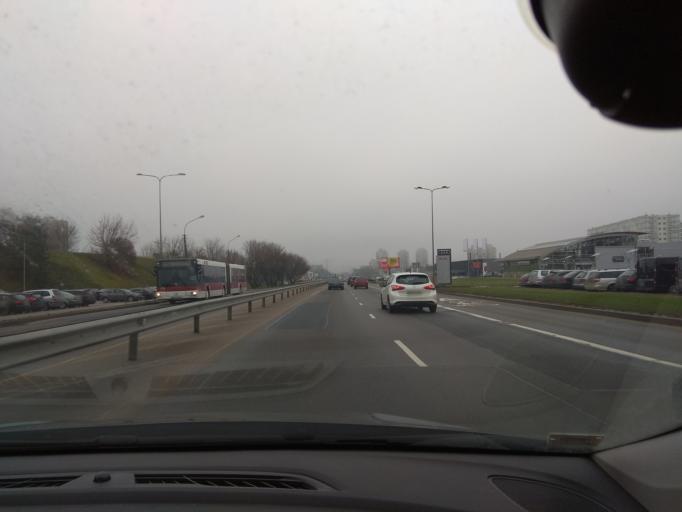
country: LT
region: Vilnius County
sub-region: Vilnius
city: Fabijoniskes
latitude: 54.7271
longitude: 25.2407
